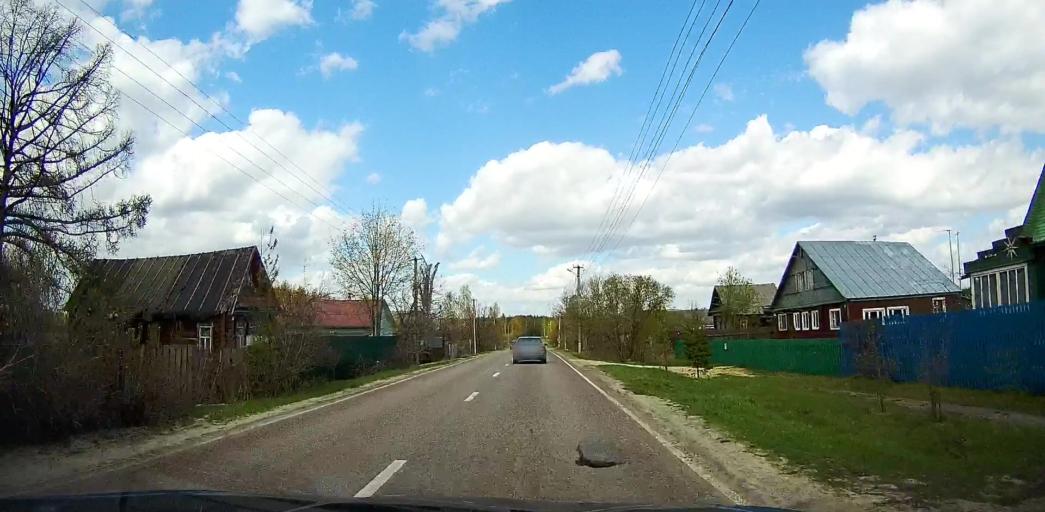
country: RU
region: Moskovskaya
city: Davydovo
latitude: 55.5862
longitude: 38.8287
